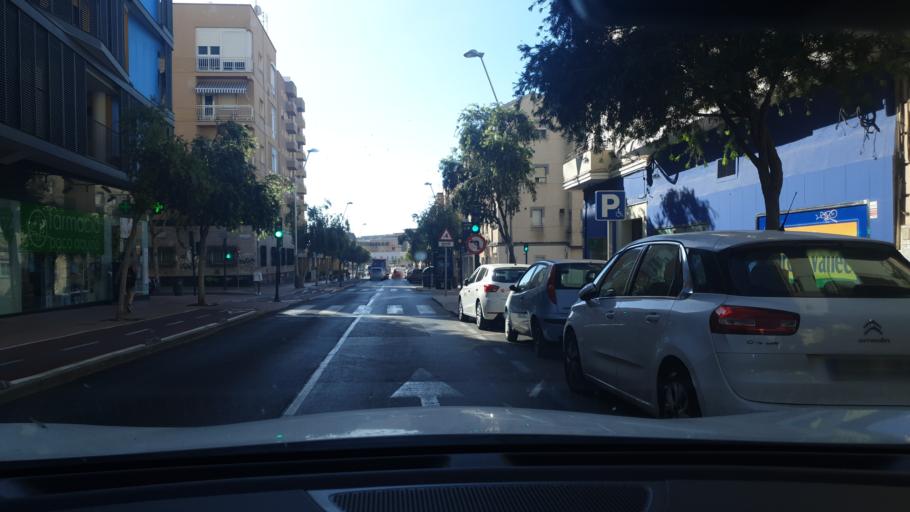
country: ES
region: Andalusia
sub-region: Provincia de Almeria
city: Almeria
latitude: 36.8403
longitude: -2.4559
